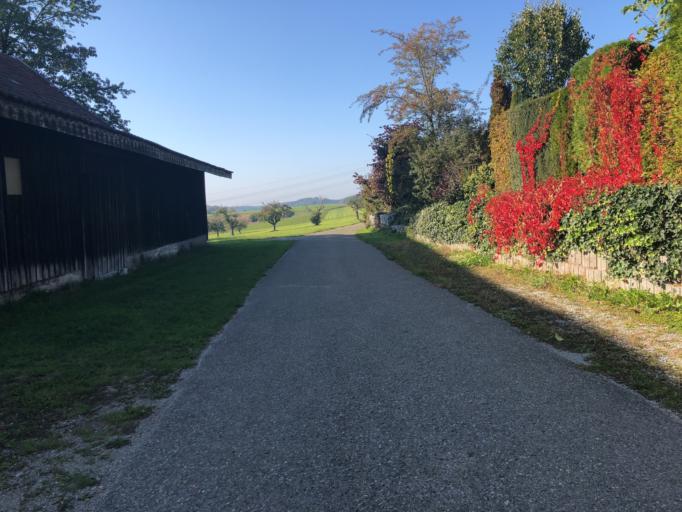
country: CH
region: Zurich
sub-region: Bezirk Uster
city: Gutenswil
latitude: 47.3862
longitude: 8.7150
